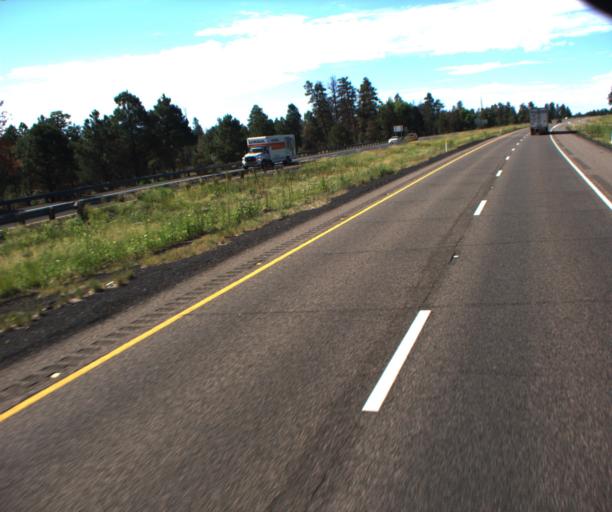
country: US
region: Arizona
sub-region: Coconino County
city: Sedona
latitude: 34.9118
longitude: -111.6413
